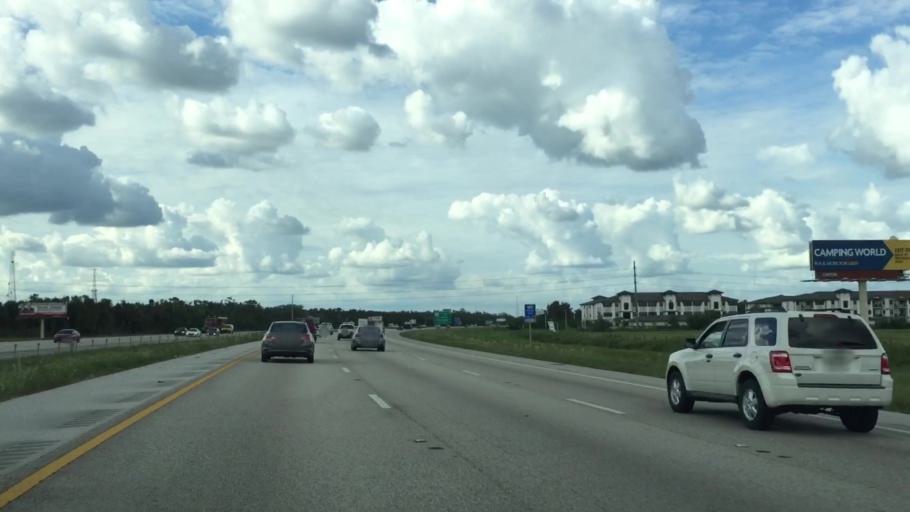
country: US
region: Florida
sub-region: Lee County
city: Fort Myers
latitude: 26.6217
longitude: -81.8069
